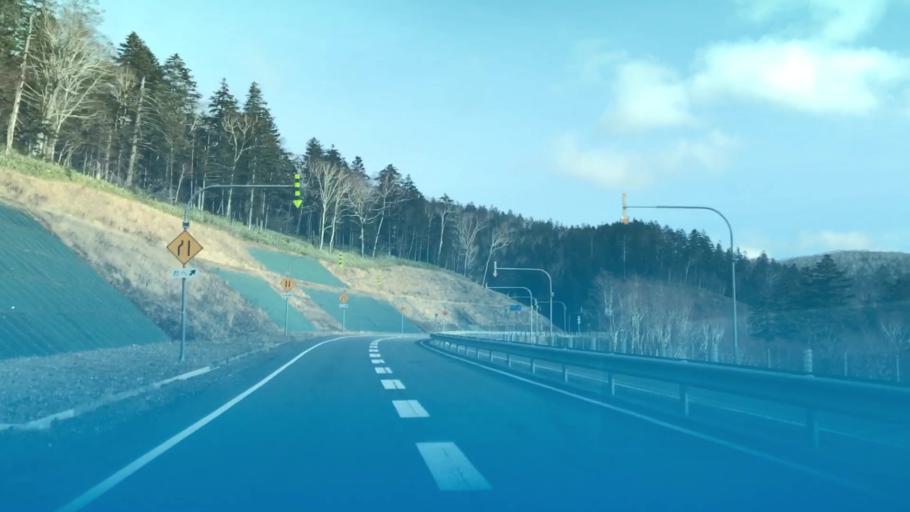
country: JP
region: Hokkaido
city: Otofuke
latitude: 42.9824
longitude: 142.7382
